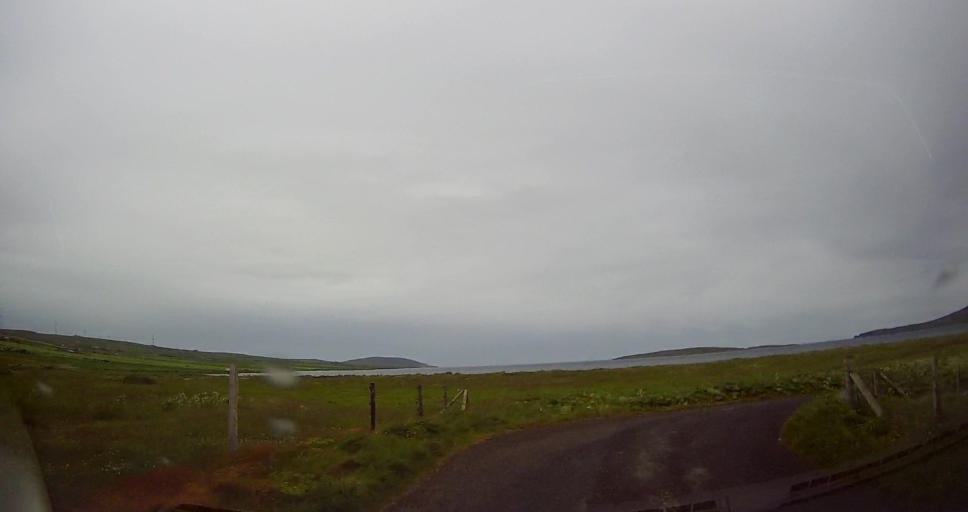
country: GB
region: Scotland
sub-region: Orkney Islands
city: Orkney
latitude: 59.1181
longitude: -3.0860
